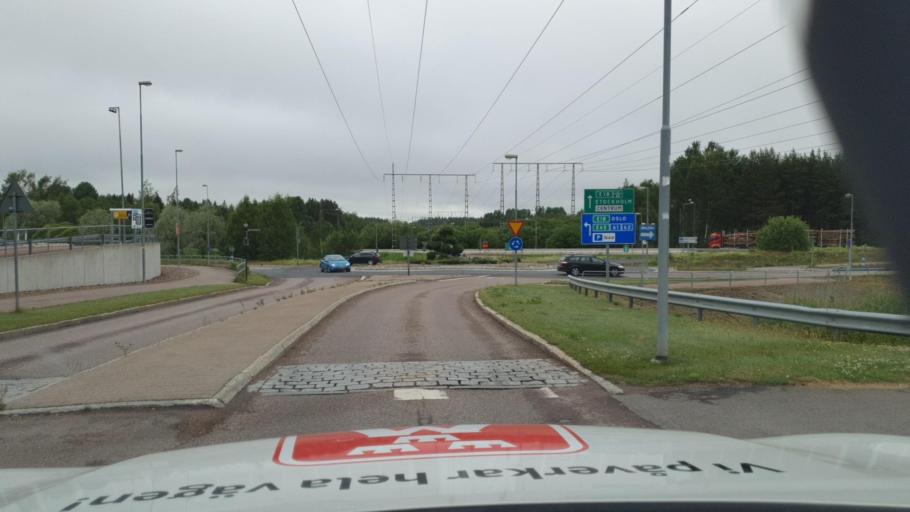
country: SE
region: Vaermland
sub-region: Hammaro Kommun
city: Skoghall
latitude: 59.3792
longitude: 13.4222
